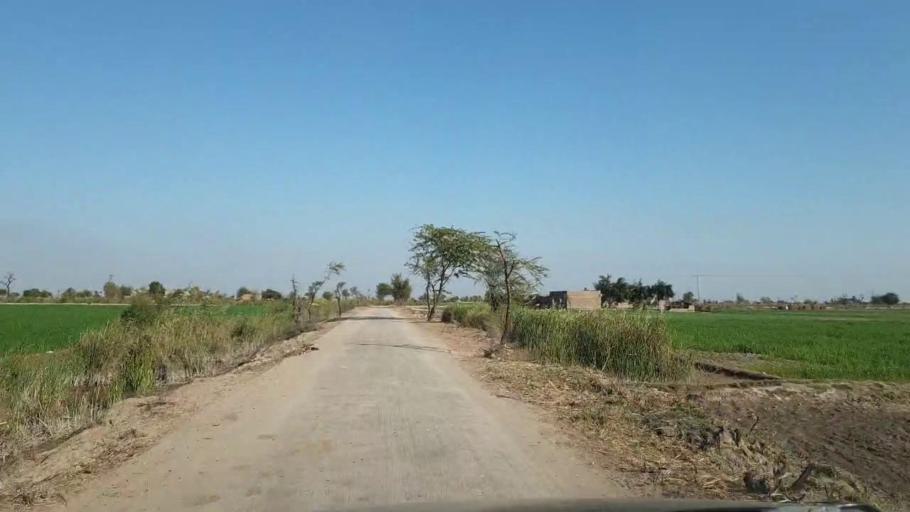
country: PK
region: Sindh
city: Khadro
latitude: 26.1645
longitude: 68.7614
